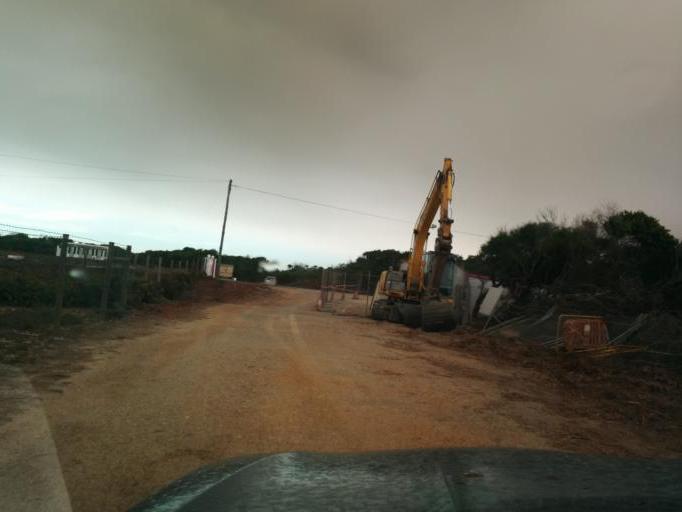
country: PT
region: Beja
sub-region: Odemira
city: Vila Nova de Milfontes
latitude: 37.5982
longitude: -8.8156
